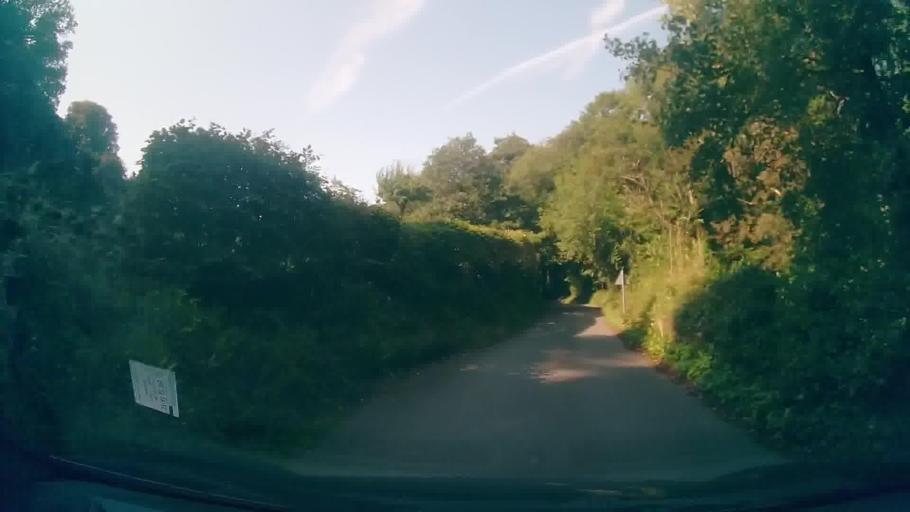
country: GB
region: Wales
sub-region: Pembrokeshire
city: Saundersfoot
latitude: 51.7420
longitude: -4.6741
